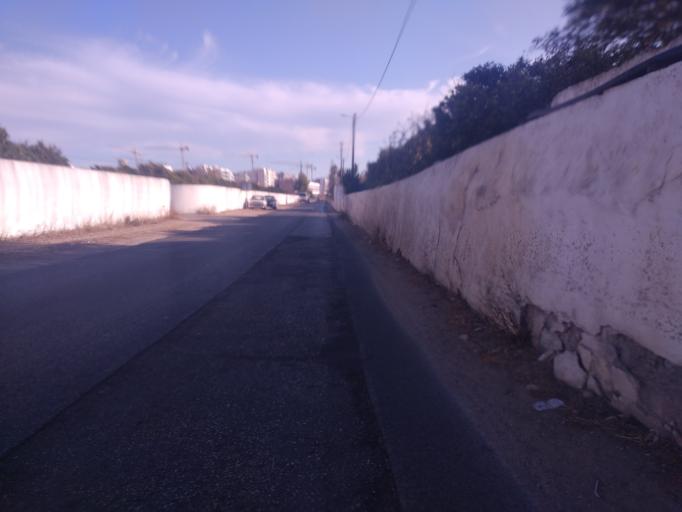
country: PT
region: Faro
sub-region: Faro
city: Faro
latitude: 37.0375
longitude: -7.9404
